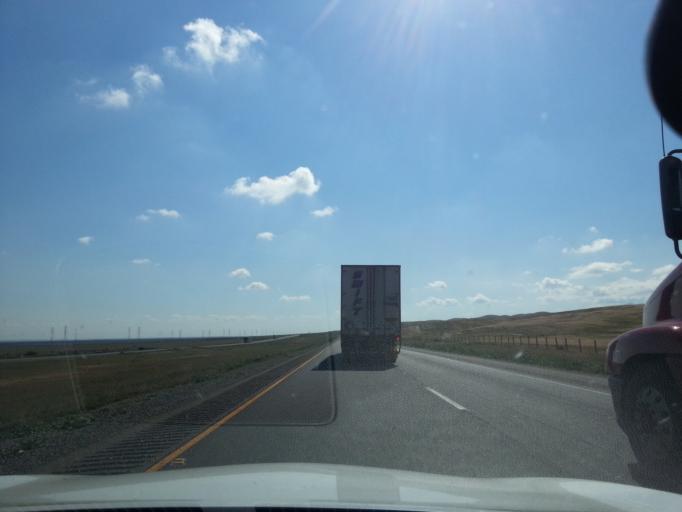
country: US
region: California
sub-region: Fresno County
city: Mendota
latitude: 36.5029
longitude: -120.4569
